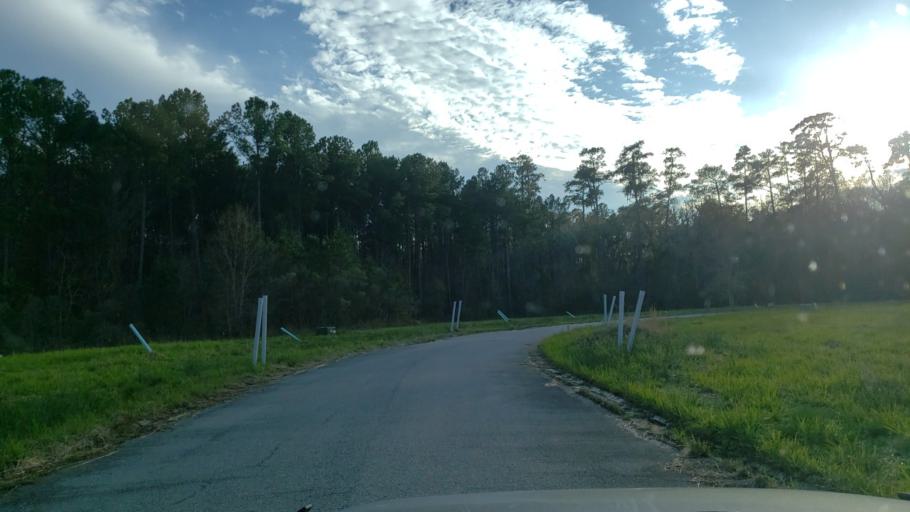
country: US
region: Georgia
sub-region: Chatham County
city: Pooler
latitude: 32.1051
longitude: -81.2388
